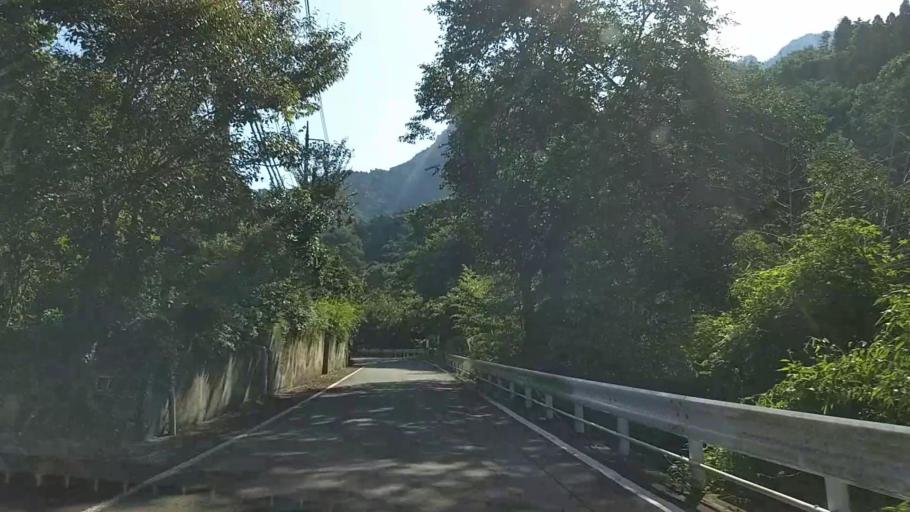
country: JP
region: Gunma
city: Annaka
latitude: 36.3240
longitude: 138.7025
